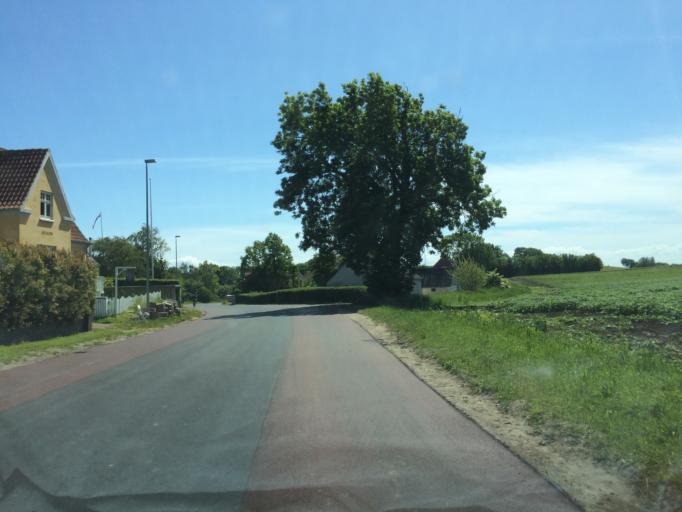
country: DK
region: Central Jutland
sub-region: Samso Kommune
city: Tranebjerg
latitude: 55.8196
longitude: 10.6050
